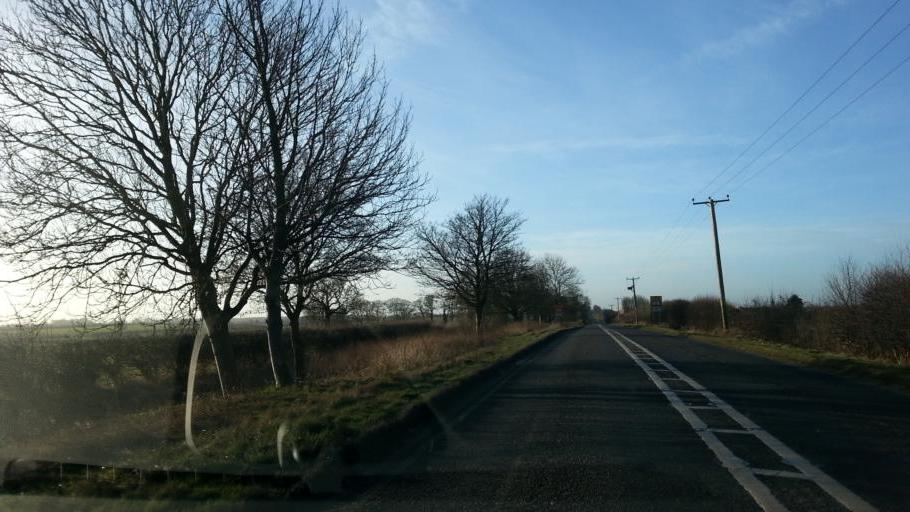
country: GB
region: England
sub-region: Lincolnshire
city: Grantham
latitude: 52.9376
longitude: -0.5650
